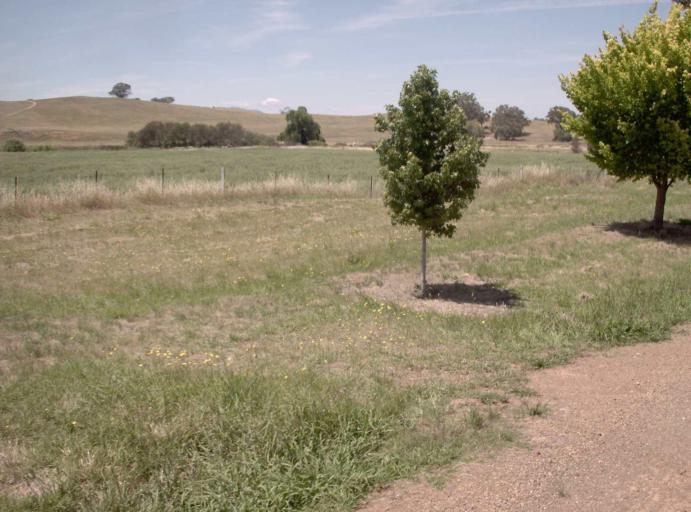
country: AU
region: Victoria
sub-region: East Gippsland
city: Bairnsdale
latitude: -37.2487
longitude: 147.7123
